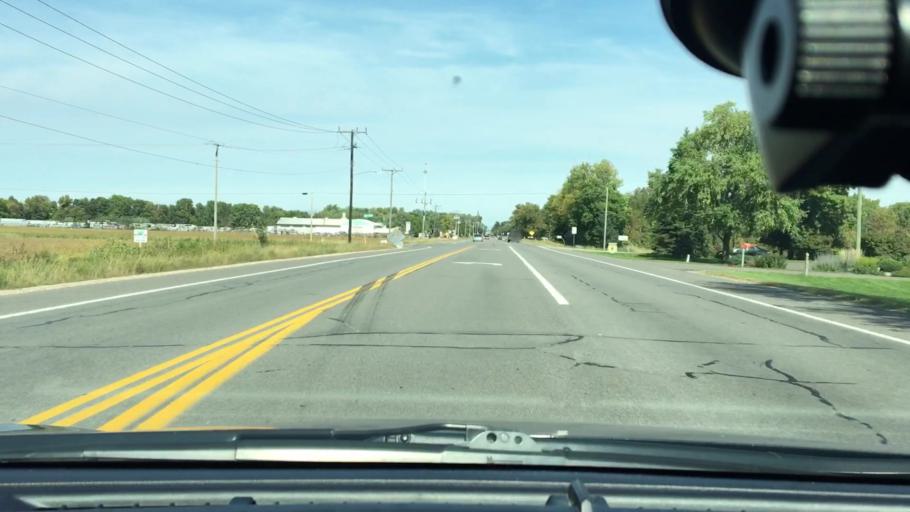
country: US
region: Minnesota
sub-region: Wright County
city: Saint Michael
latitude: 45.1948
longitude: -93.6650
